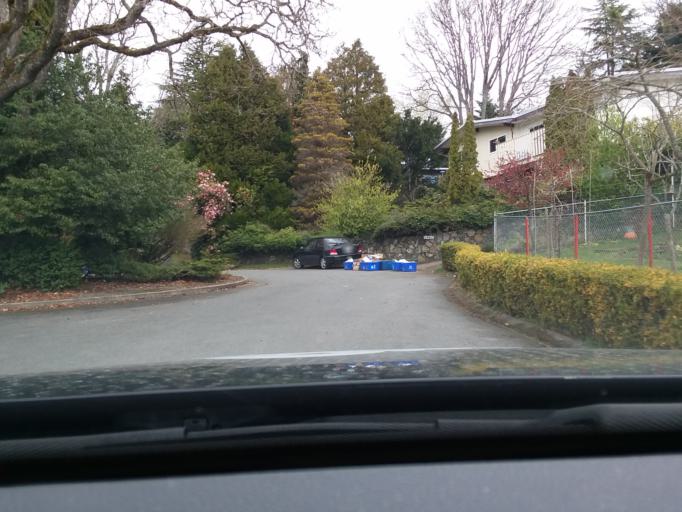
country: CA
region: British Columbia
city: Oak Bay
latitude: 48.4695
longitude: -123.3410
